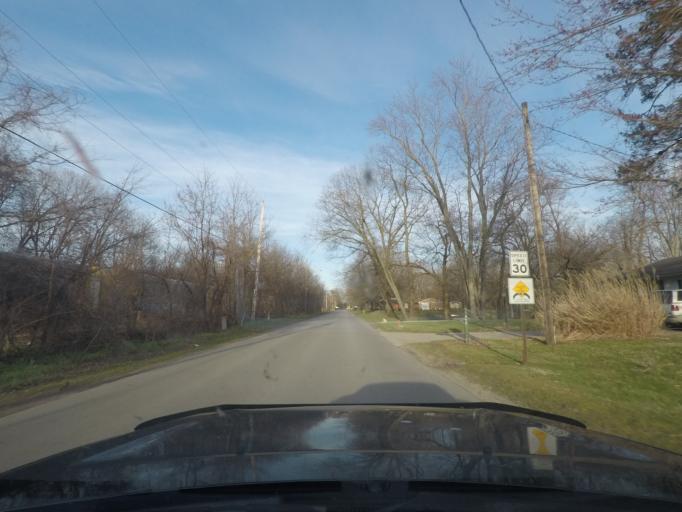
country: US
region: Indiana
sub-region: LaPorte County
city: LaPorte
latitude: 41.6046
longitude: -86.7453
